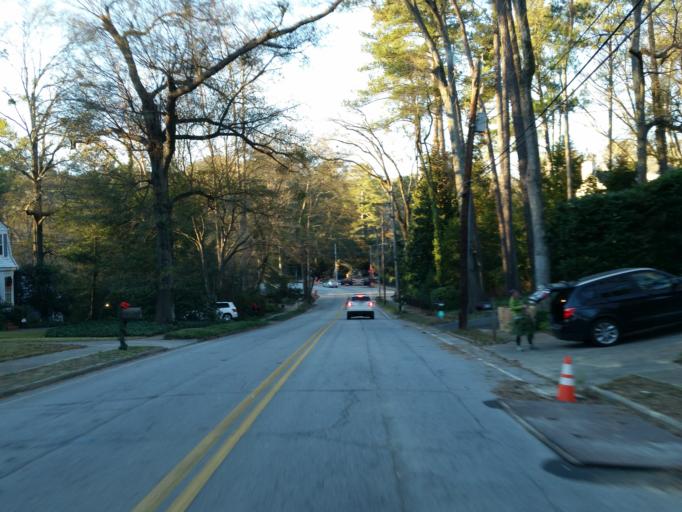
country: US
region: Georgia
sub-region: Cobb County
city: Vinings
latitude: 33.8229
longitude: -84.4065
